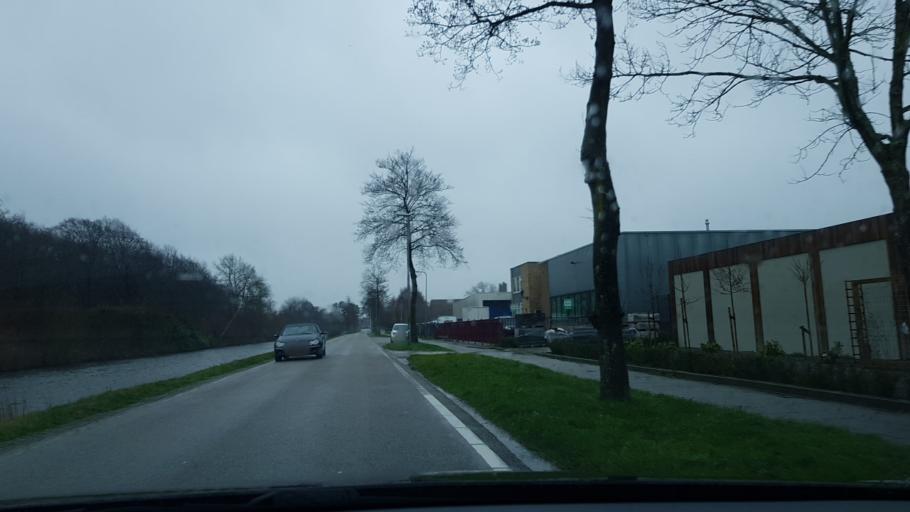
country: NL
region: North Holland
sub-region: Gemeente Bloemendaal
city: Bennebroek
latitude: 52.3314
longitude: 4.5929
